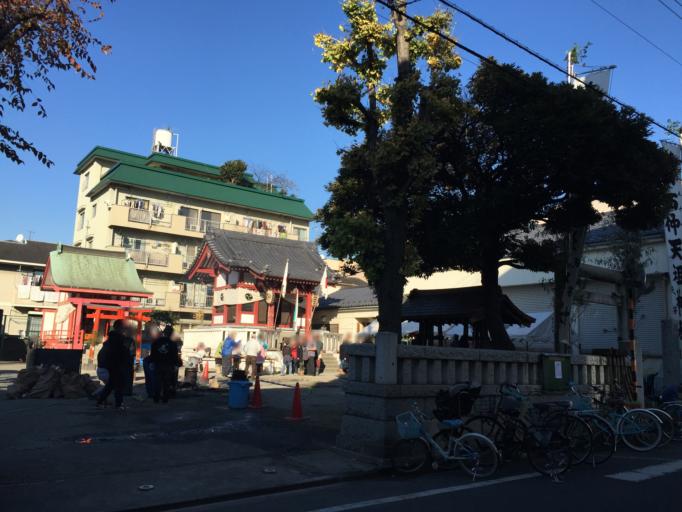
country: JP
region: Kanagawa
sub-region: Kawasaki-shi
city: Kawasaki
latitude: 35.5556
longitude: 139.7304
